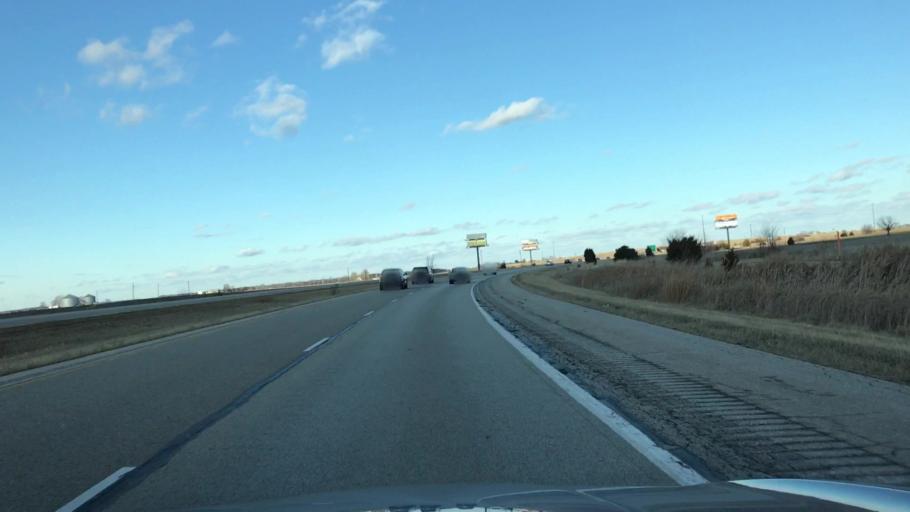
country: US
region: Illinois
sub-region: McLean County
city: Hudson
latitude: 40.5649
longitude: -88.9077
